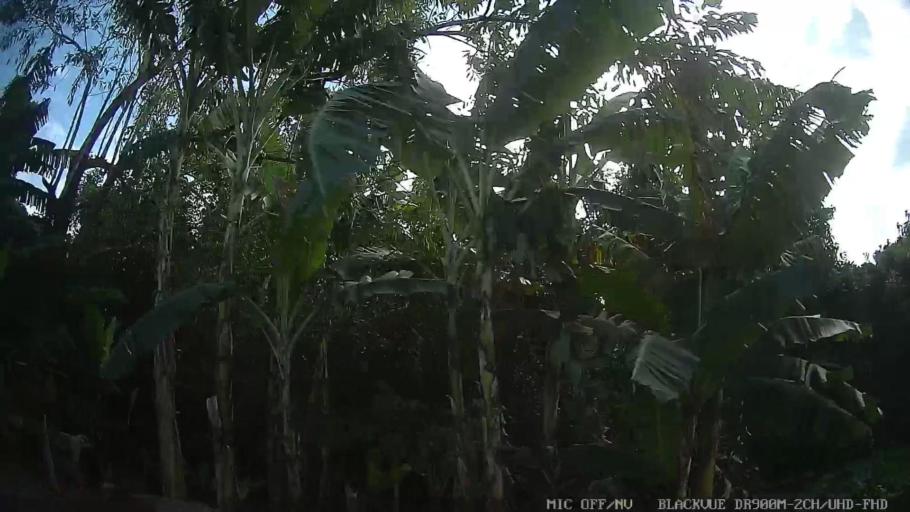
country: BR
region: Sao Paulo
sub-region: Guaruja
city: Guaruja
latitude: -23.9738
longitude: -46.2133
